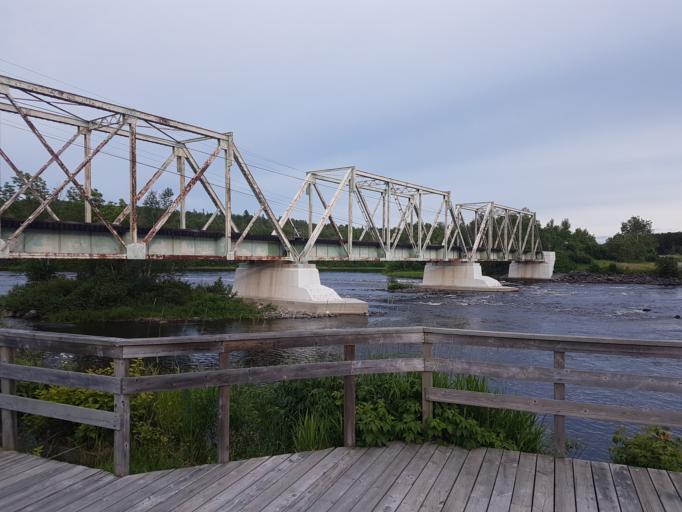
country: CA
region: Ontario
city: Temiskaming Shores
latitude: 47.3230
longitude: -79.8099
